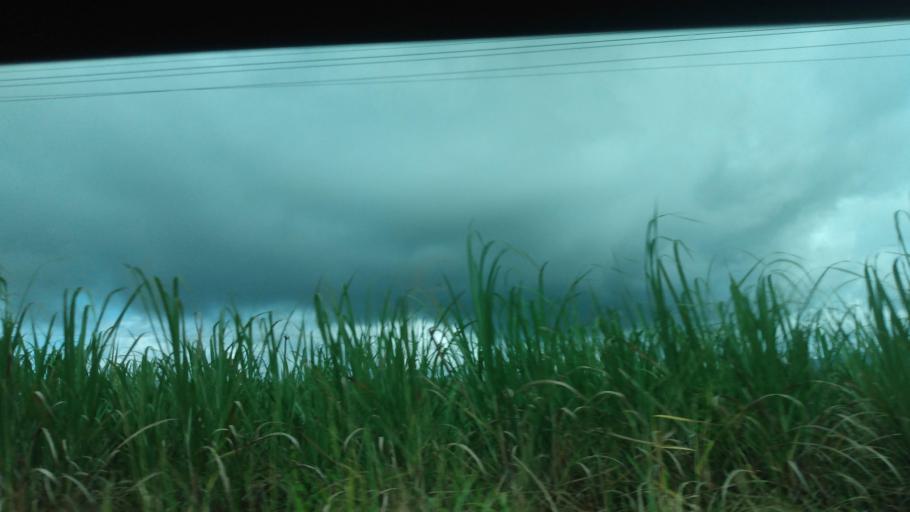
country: BR
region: Pernambuco
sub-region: Quipapa
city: Quipapa
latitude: -8.7988
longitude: -35.9979
